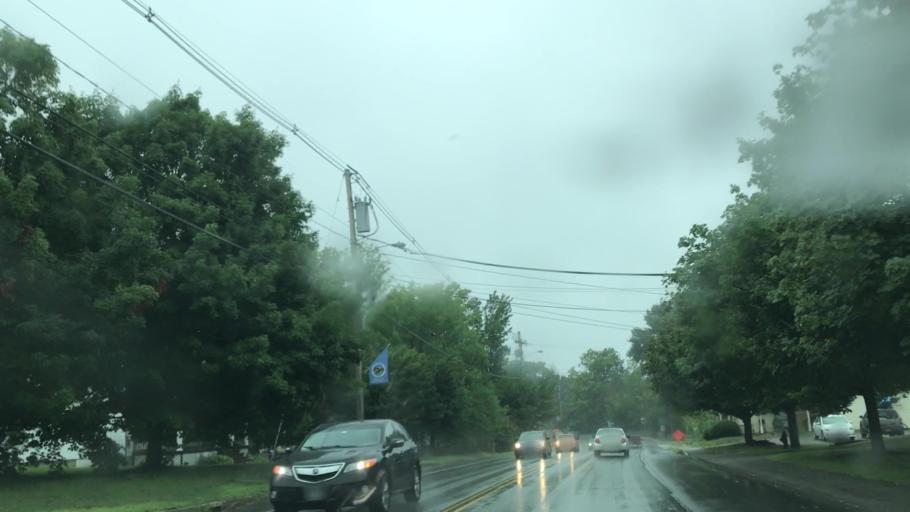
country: US
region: Maine
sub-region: York County
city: North Berwick
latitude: 43.3028
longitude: -70.7407
